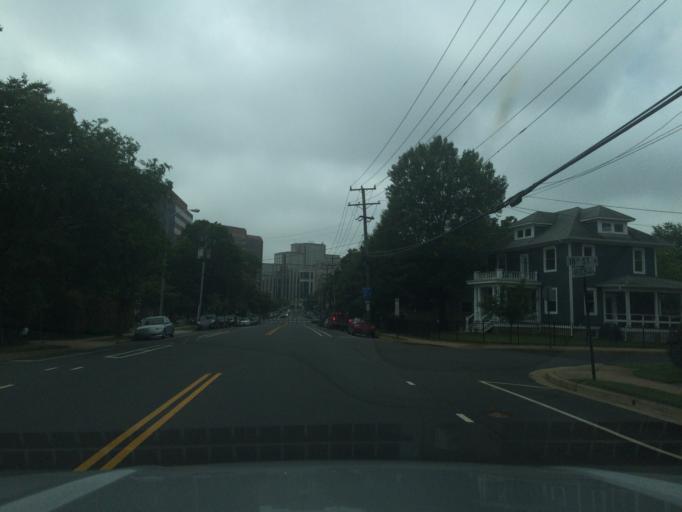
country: US
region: Virginia
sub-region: Arlington County
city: Arlington
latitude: 38.8950
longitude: -77.0863
